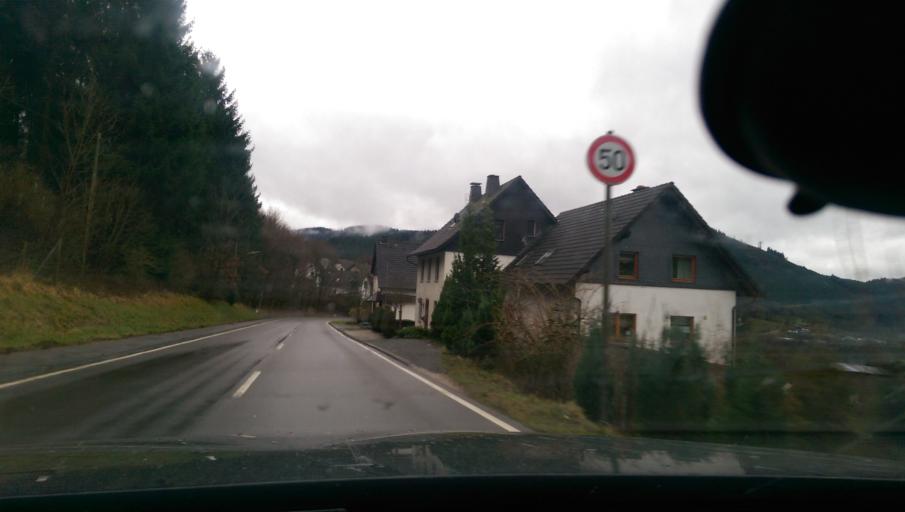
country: DE
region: North Rhine-Westphalia
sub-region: Regierungsbezirk Arnsberg
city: Finnentrop
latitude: 51.2256
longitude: 7.9593
